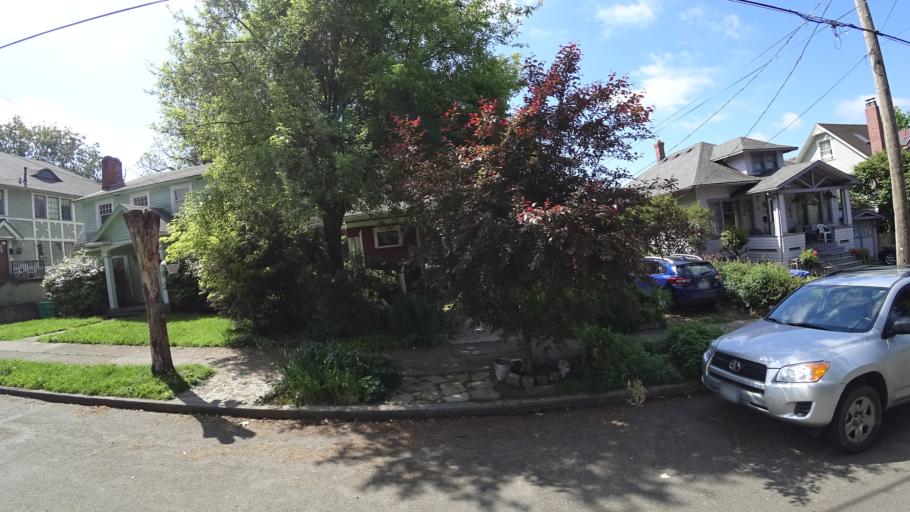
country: US
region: Oregon
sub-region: Multnomah County
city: Portland
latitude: 45.5136
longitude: -122.6409
